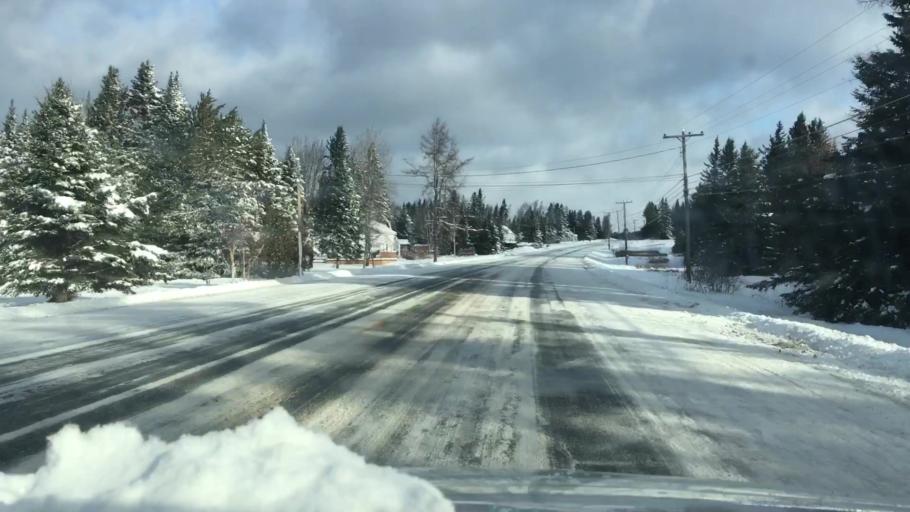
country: US
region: Maine
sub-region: Aroostook County
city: Madawaska
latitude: 47.0045
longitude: -68.0230
